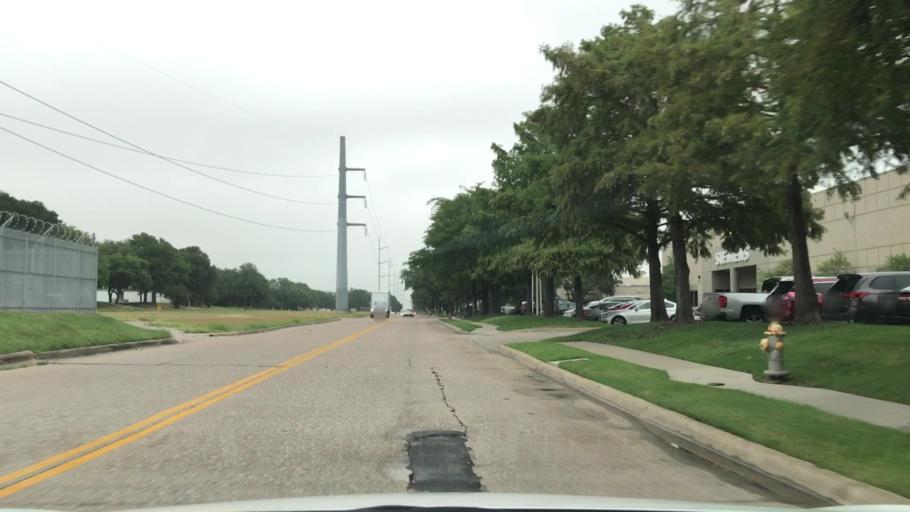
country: US
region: Texas
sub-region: Dallas County
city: Coppell
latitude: 32.9264
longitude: -97.0199
